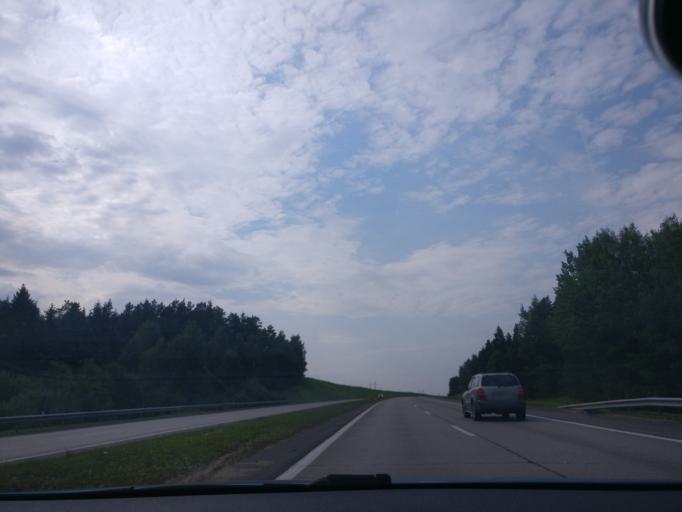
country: BY
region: Minsk
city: Astrashytski Haradok
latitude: 54.1054
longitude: 27.7987
